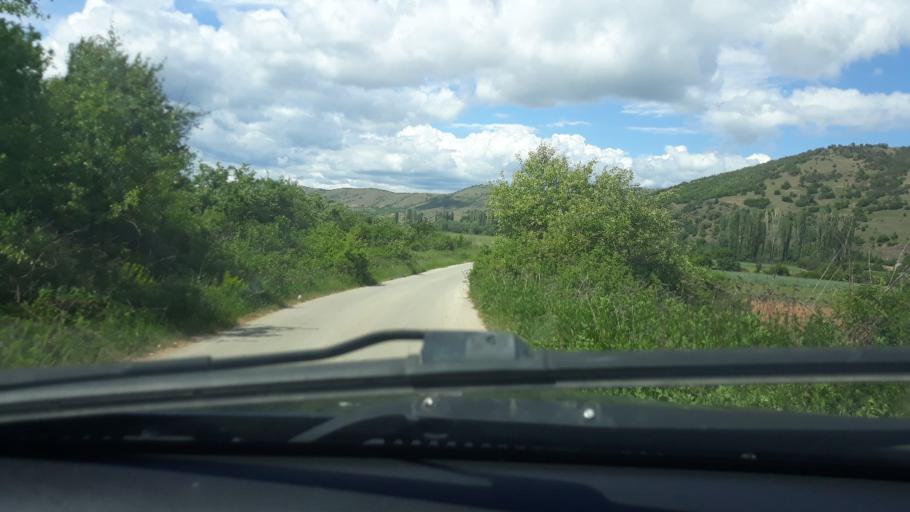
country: MK
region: Krivogastani
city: Krivogashtani
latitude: 41.3518
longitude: 21.2972
